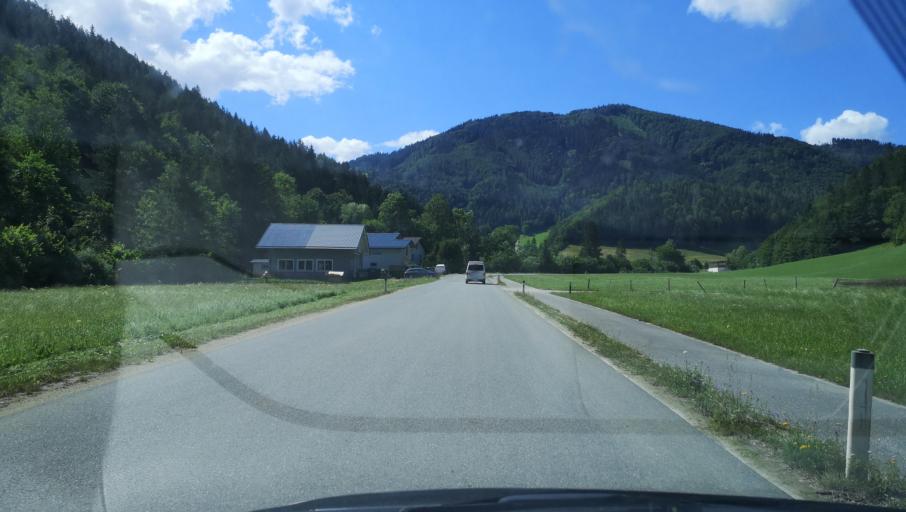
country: AT
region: Lower Austria
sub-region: Politischer Bezirk Scheibbs
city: Gresten
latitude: 47.9371
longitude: 15.0283
